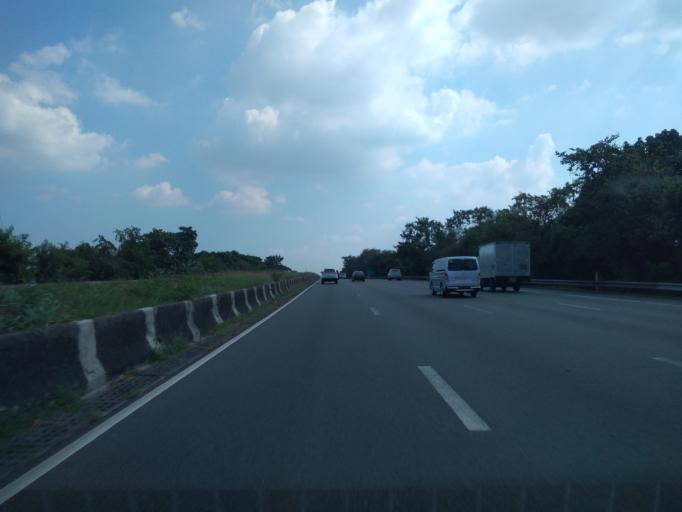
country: PH
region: Calabarzon
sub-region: Province of Laguna
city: San Pedro
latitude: 14.3475
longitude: 121.0471
